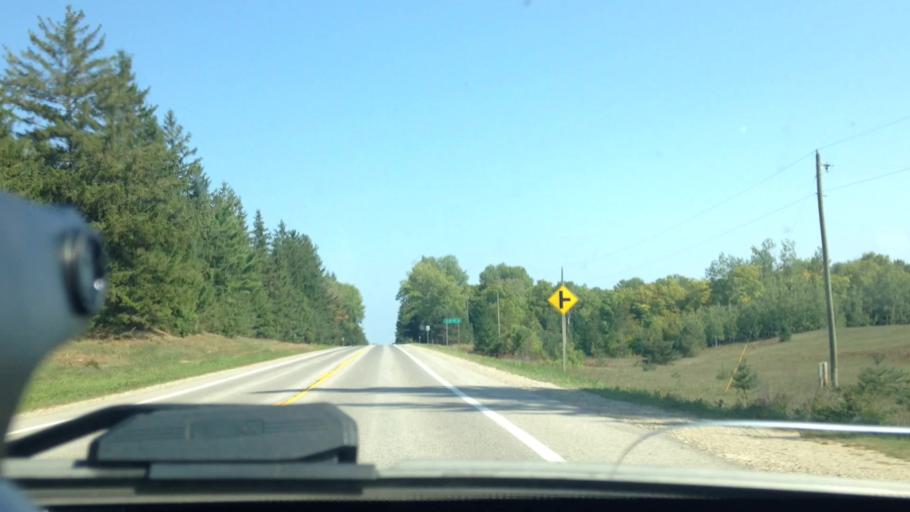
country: US
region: Michigan
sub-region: Luce County
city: Newberry
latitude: 46.3037
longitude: -85.4411
